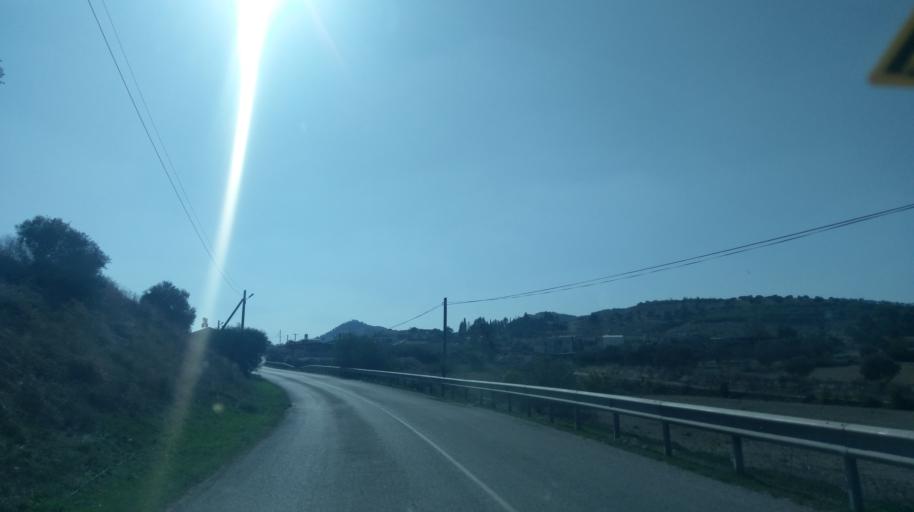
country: CY
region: Lefkosia
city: Lympia
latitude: 35.0192
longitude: 33.4664
